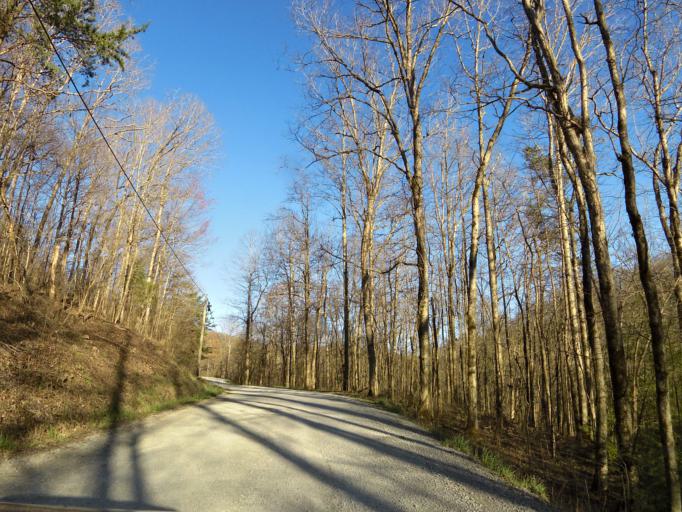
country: US
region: Tennessee
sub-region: Campbell County
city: Caryville
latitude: 36.2501
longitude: -84.3432
